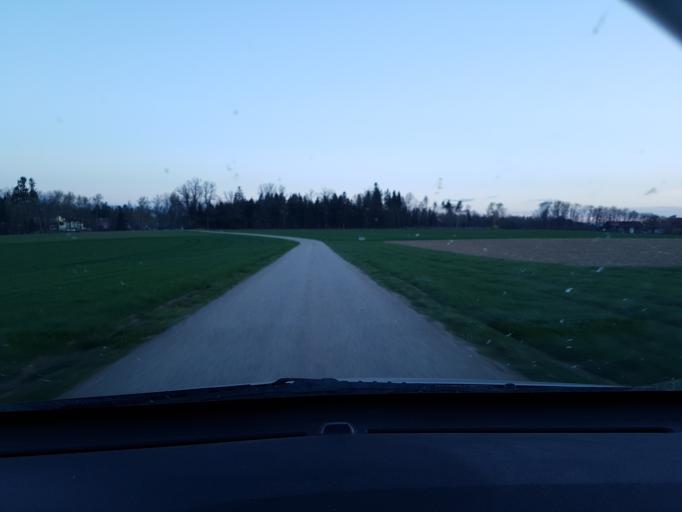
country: AT
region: Upper Austria
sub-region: Politischer Bezirk Linz-Land
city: Ansfelden
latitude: 48.1684
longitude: 14.3203
